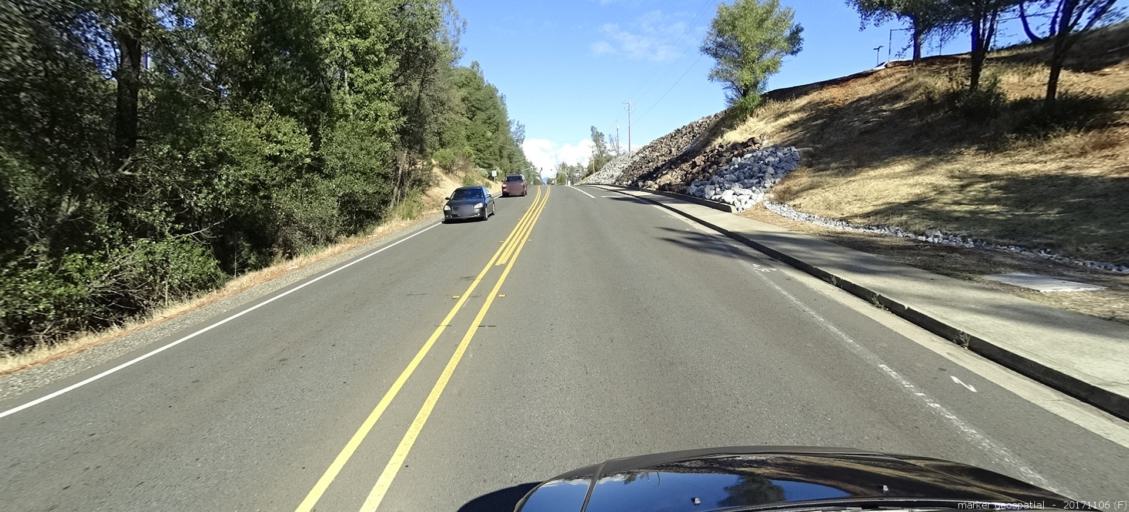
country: US
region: California
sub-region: Shasta County
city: Palo Cedro
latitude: 40.5686
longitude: -122.2386
